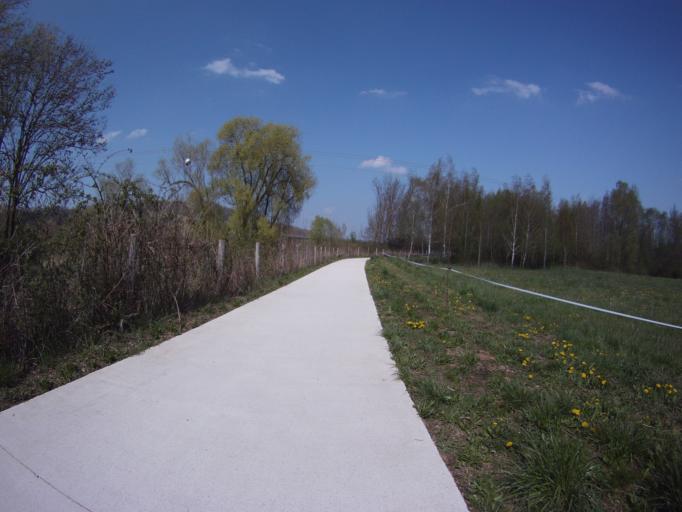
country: FR
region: Lorraine
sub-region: Departement de Meurthe-et-Moselle
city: Dieulouard
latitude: 48.8468
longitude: 6.0801
